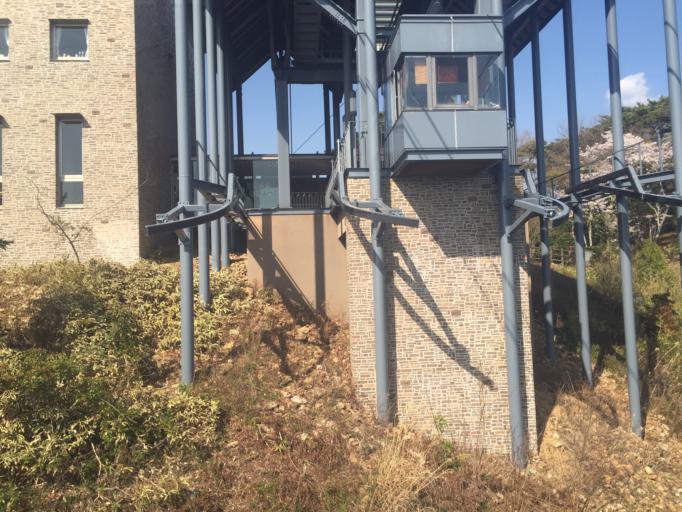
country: JP
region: Shizuoka
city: Kosai-shi
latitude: 34.7695
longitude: 137.6204
